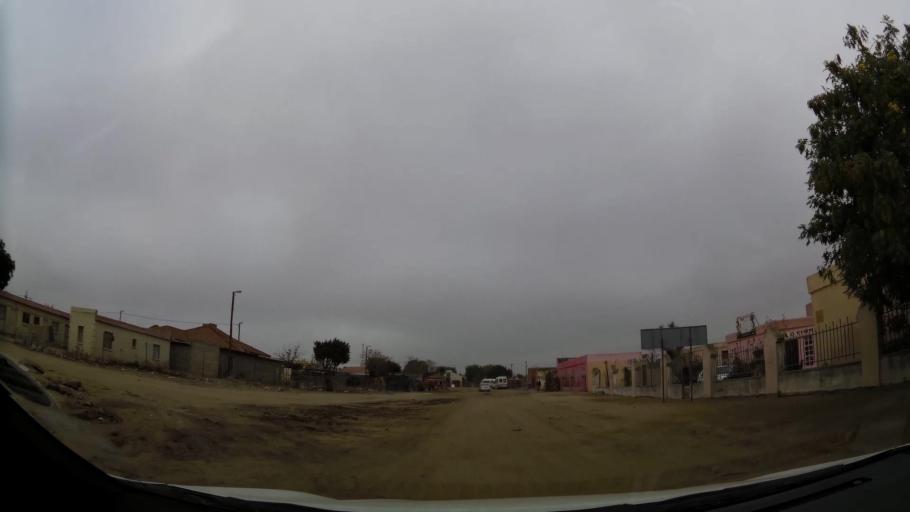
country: ZA
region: Limpopo
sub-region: Capricorn District Municipality
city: Polokwane
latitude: -23.8340
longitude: 29.3894
